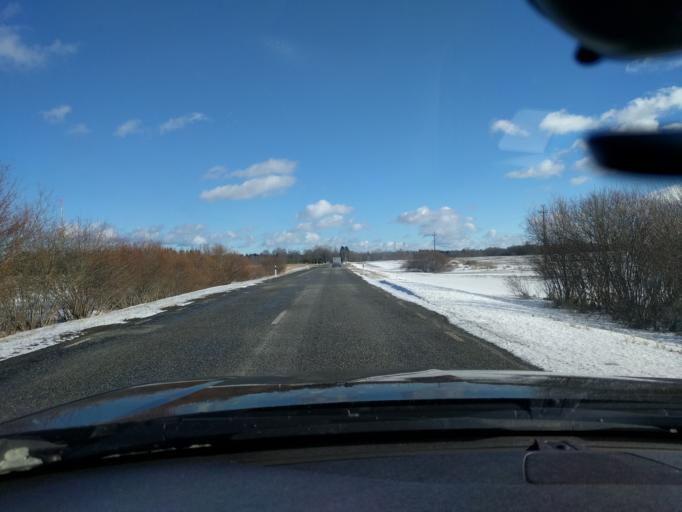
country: EE
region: Harju
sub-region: Raasiku vald
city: Raasiku
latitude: 59.4121
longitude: 25.2286
